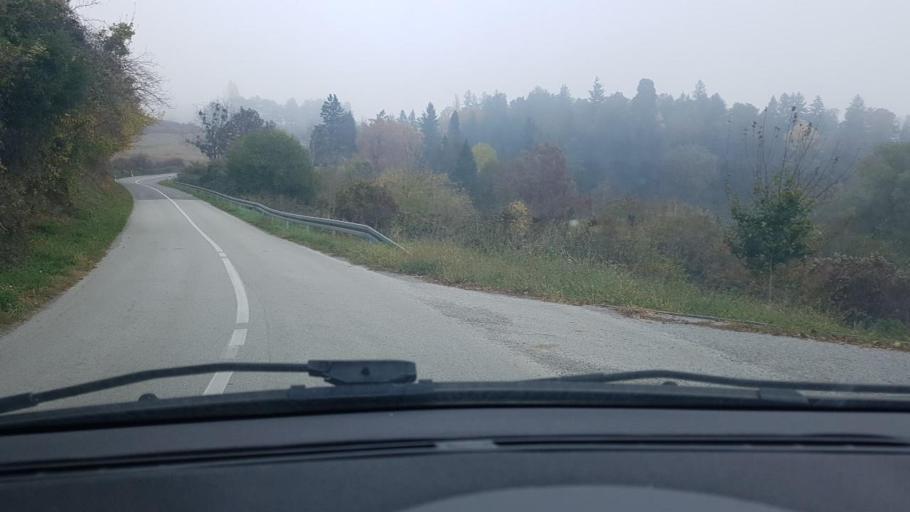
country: HR
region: Varazdinska
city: Ivanec
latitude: 46.1423
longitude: 16.1592
